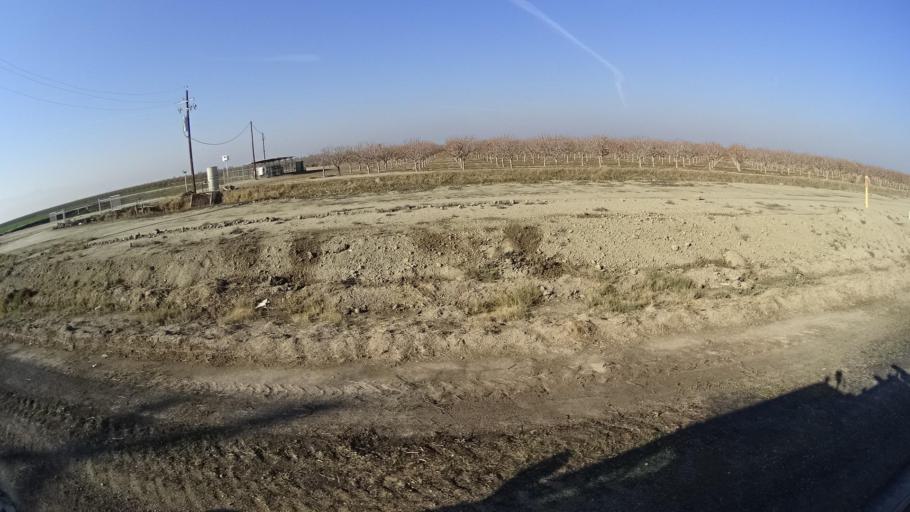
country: US
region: California
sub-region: Kern County
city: Weedpatch
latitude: 35.2016
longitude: -118.9677
